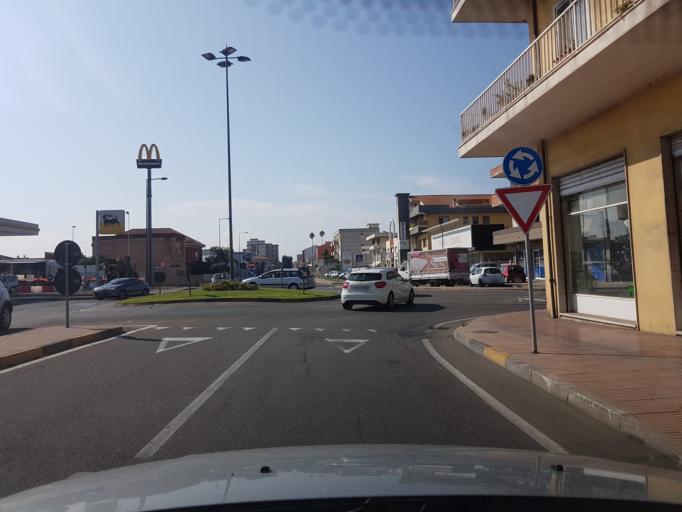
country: IT
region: Sardinia
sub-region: Provincia di Oristano
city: Oristano
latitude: 39.9123
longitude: 8.5872
